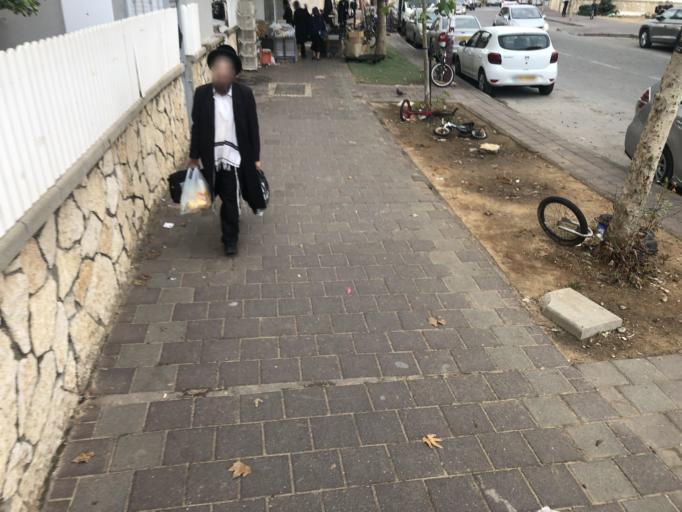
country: IL
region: Jerusalem
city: Modiin Ilit
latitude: 31.9383
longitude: 35.0441
